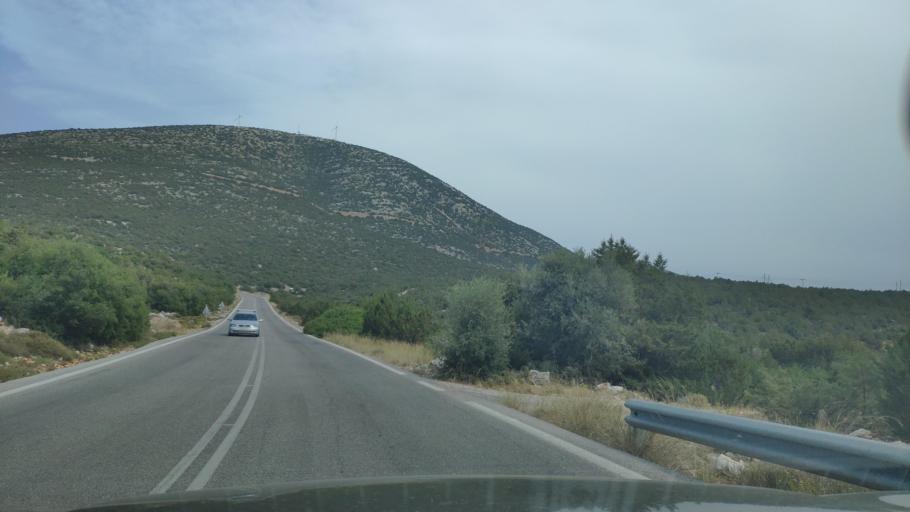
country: GR
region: Peloponnese
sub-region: Nomos Argolidos
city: Didyma
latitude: 37.5058
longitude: 23.1875
